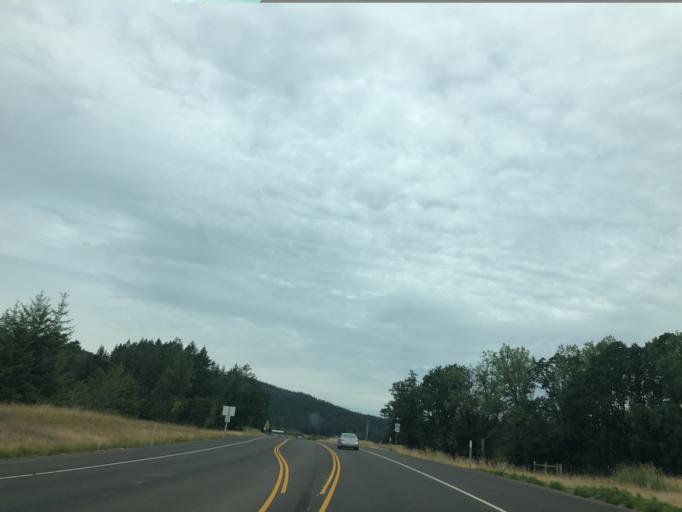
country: US
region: Oregon
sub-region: Benton County
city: Philomath
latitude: 44.5882
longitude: -123.4306
